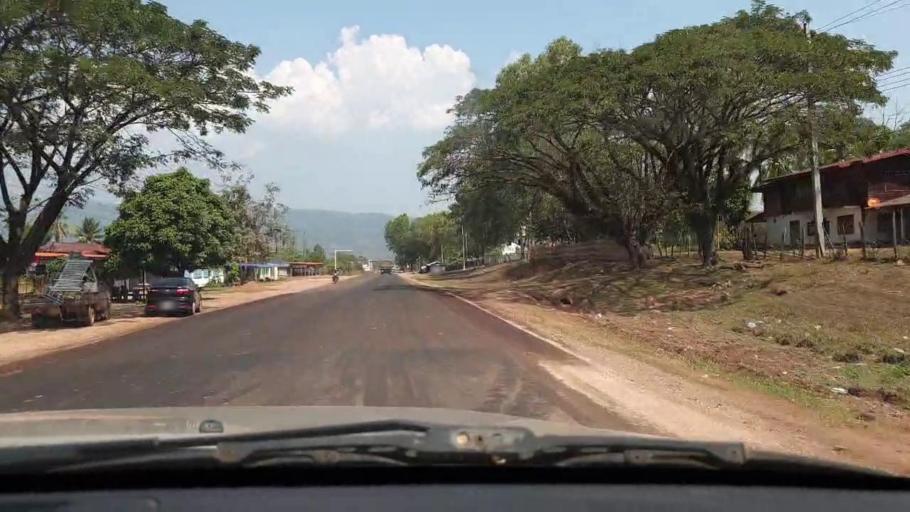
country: TH
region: Nong Khai
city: Rattanawapi
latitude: 18.1864
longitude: 103.0552
